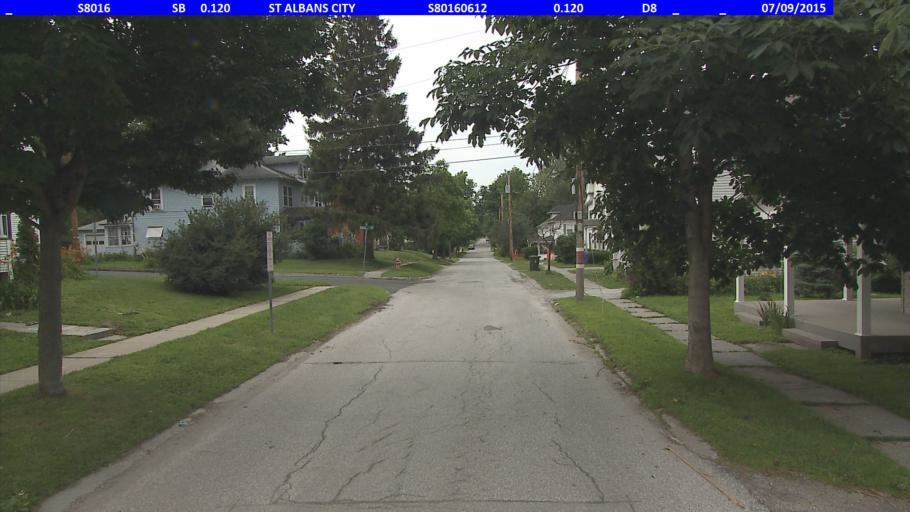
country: US
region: Vermont
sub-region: Franklin County
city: Saint Albans
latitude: 44.8075
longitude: -73.0812
